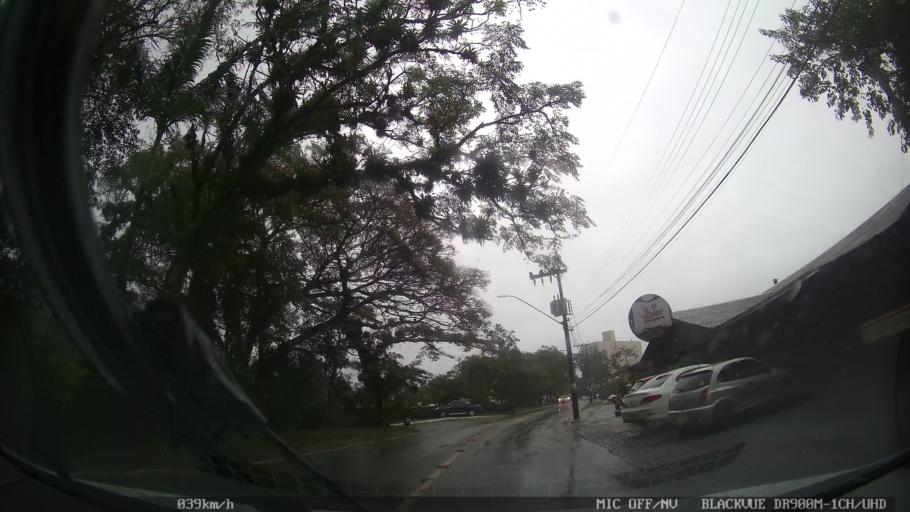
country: BR
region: Santa Catarina
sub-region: Balneario Camboriu
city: Balneario Camboriu
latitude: -27.0108
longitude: -48.6249
